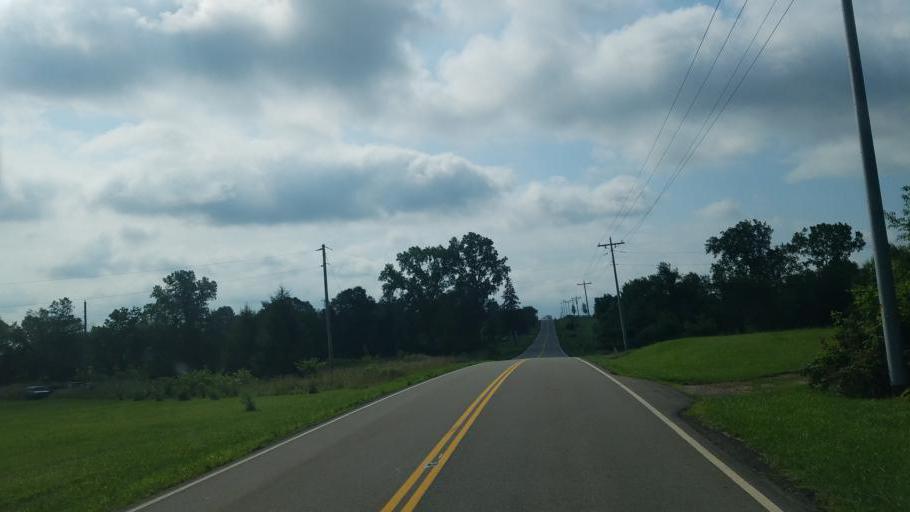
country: US
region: Ohio
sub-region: Knox County
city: Centerburg
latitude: 40.2447
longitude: -82.5813
